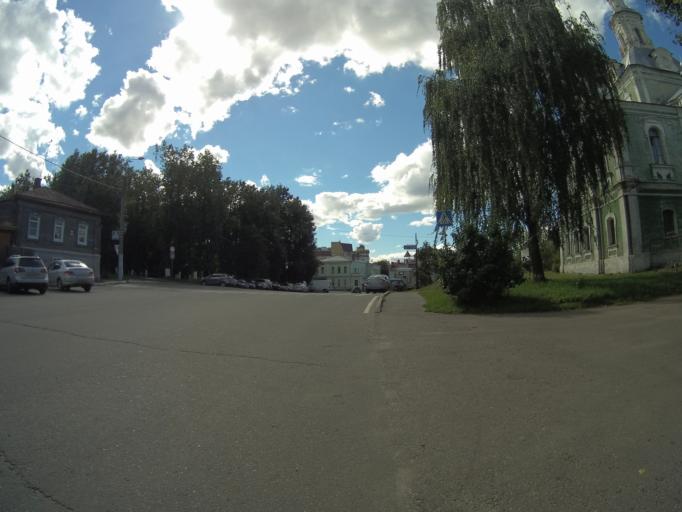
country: RU
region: Vladimir
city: Vladimir
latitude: 56.1305
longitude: 40.3984
